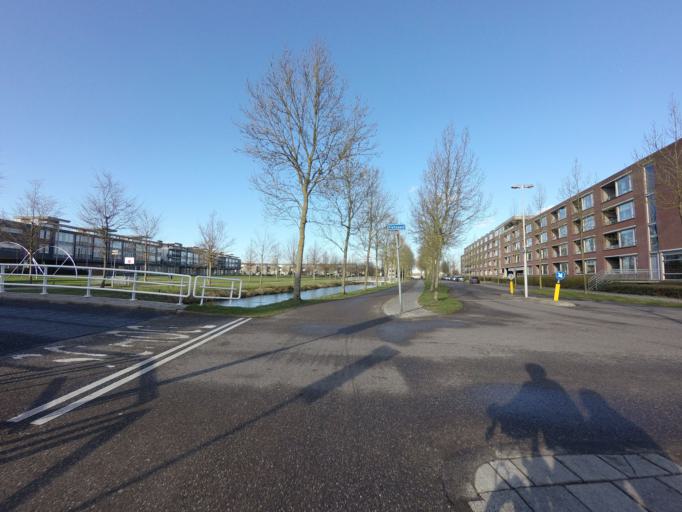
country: NL
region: Utrecht
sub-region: Stichtse Vecht
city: Spechtenkamp
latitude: 52.1072
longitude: 5.0210
